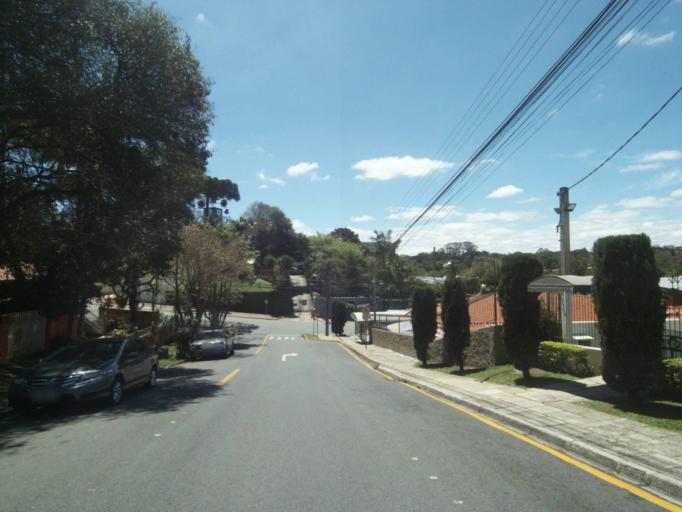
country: BR
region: Parana
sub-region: Curitiba
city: Curitiba
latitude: -25.3902
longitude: -49.2690
